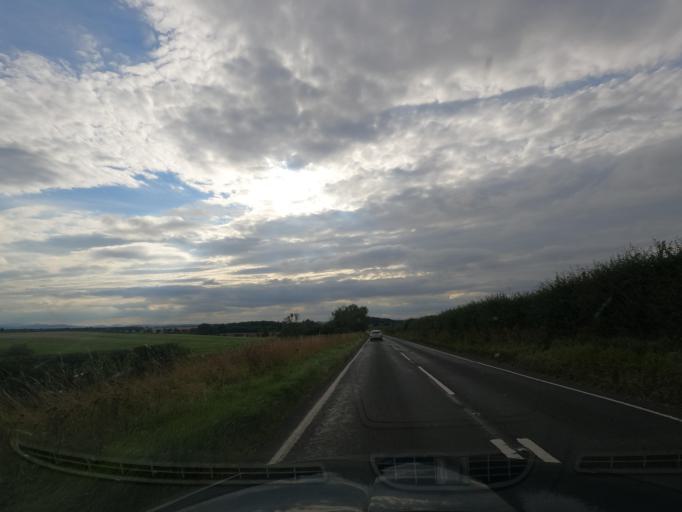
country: GB
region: England
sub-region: Northumberland
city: Ford
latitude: 55.7077
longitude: -2.1387
